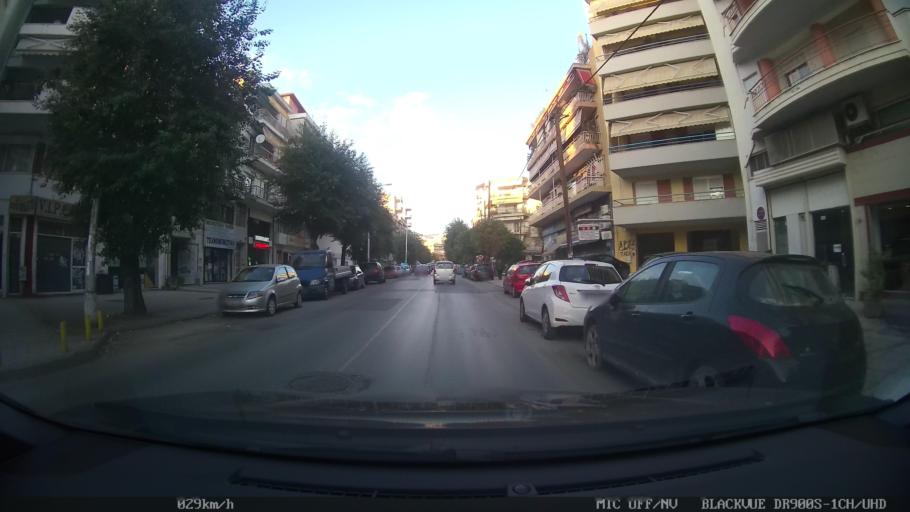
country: GR
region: Central Macedonia
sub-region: Nomos Thessalonikis
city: Triandria
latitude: 40.6059
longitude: 22.9750
